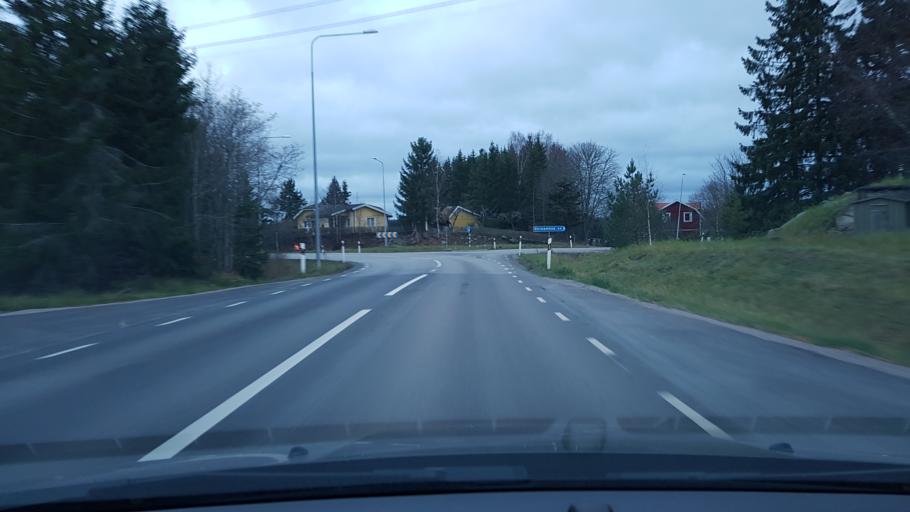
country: SE
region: Uppsala
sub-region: Uppsala Kommun
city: Vattholma
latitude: 59.9521
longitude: 17.8975
